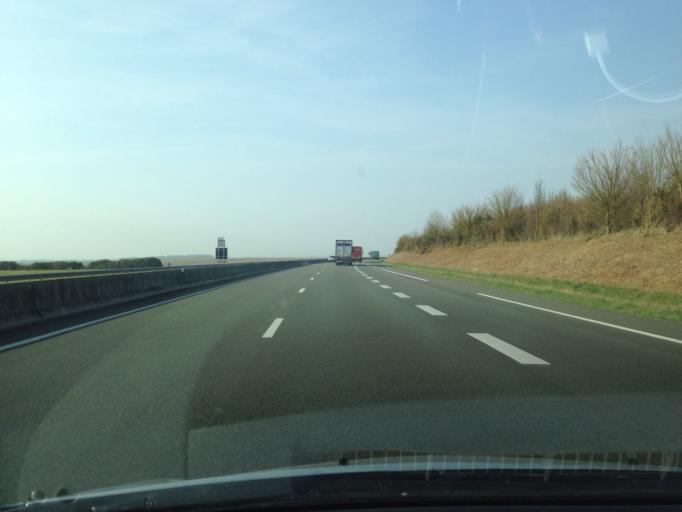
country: FR
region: Picardie
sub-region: Departement de la Somme
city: Sailly-Flibeaucourt
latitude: 50.1707
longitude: 1.7554
